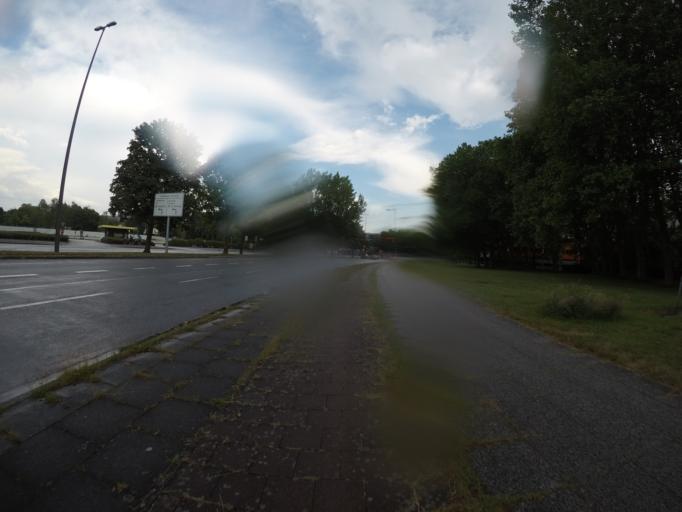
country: DE
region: Hamburg
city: Alsterdorf
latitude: 53.6065
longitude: 10.0240
